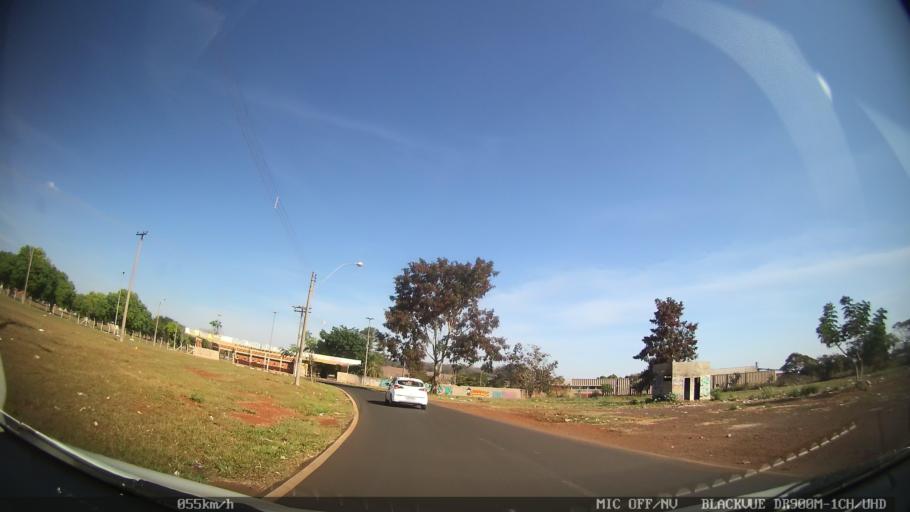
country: BR
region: Sao Paulo
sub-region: Ribeirao Preto
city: Ribeirao Preto
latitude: -21.1489
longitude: -47.7714
